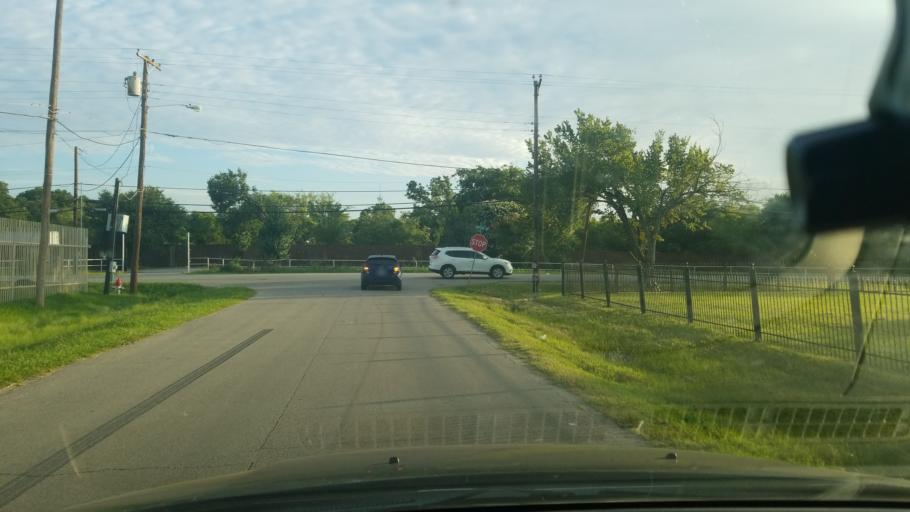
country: US
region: Texas
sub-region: Dallas County
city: Balch Springs
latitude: 32.7483
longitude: -96.6349
